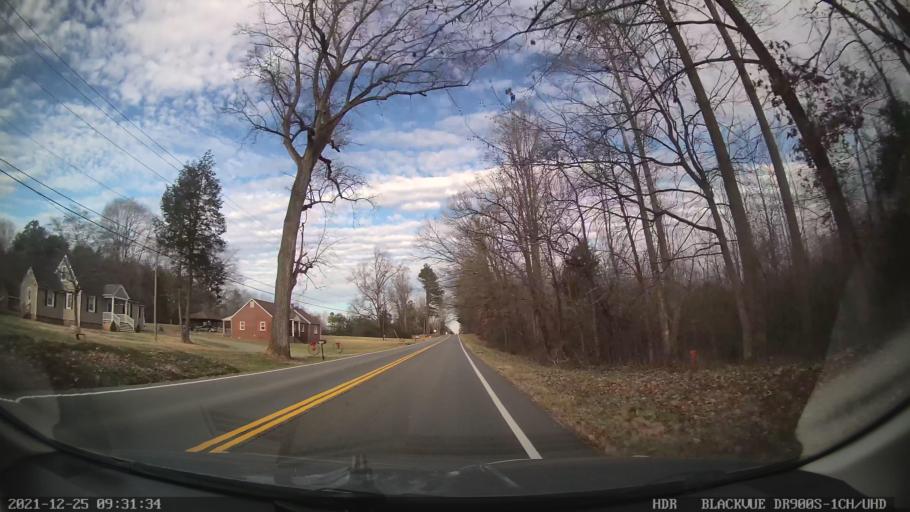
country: US
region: Virginia
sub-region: Goochland County
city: Goochland
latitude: 37.7165
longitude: -77.8230
